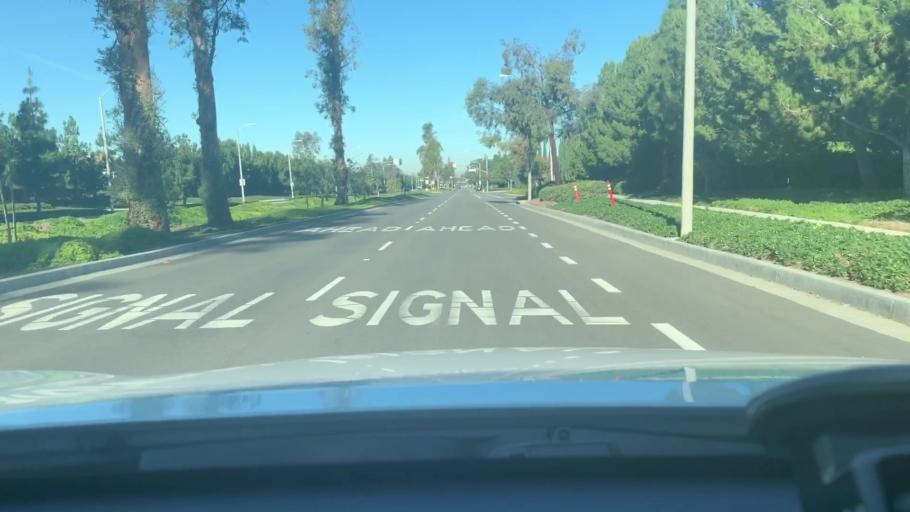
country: US
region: California
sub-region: Orange County
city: Irvine
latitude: 33.6897
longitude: -117.7525
